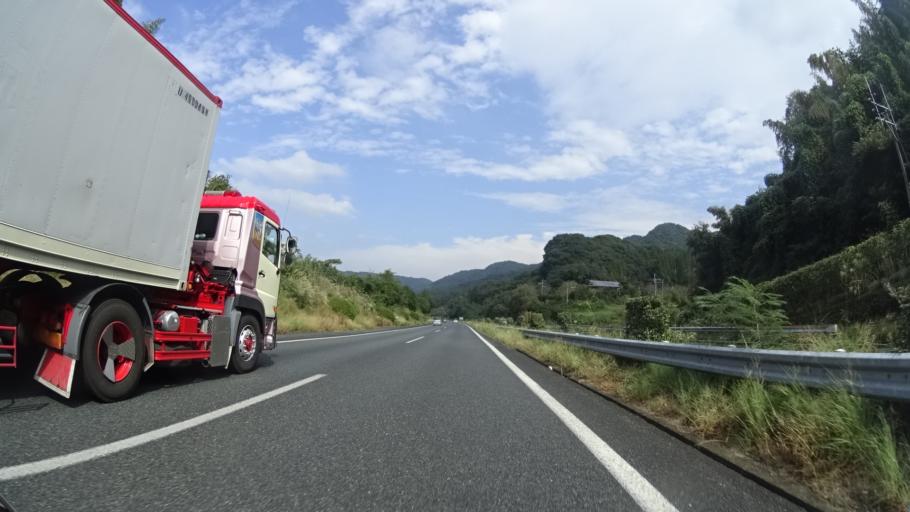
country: JP
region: Kumamoto
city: Matsubase
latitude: 32.5967
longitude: 130.7181
